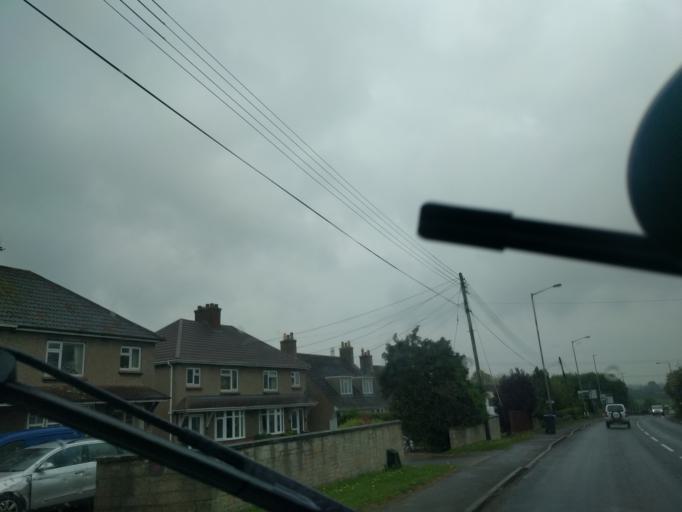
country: GB
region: England
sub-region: Wiltshire
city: Chippenham
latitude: 51.4766
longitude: -2.1275
